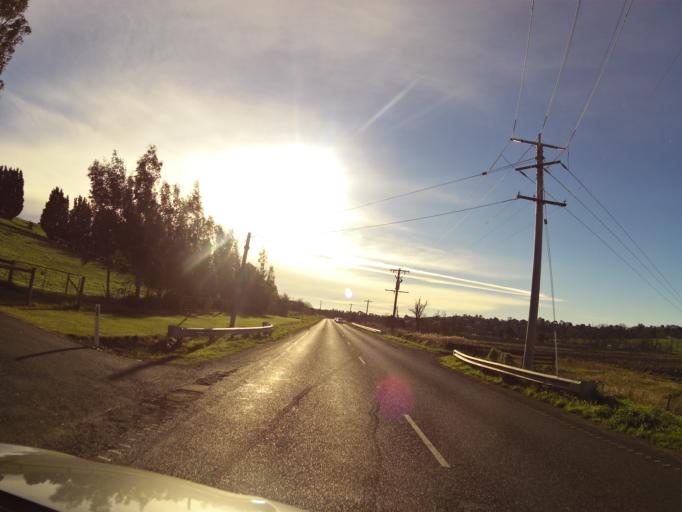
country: AU
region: Victoria
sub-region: Yarra Ranges
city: Lysterfield
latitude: -37.9093
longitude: 145.2950
